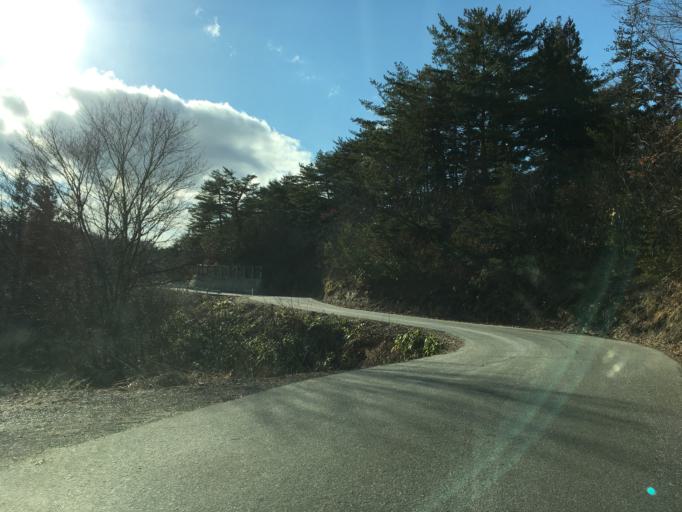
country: JP
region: Yamagata
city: Yonezawa
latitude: 37.9273
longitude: 139.9481
